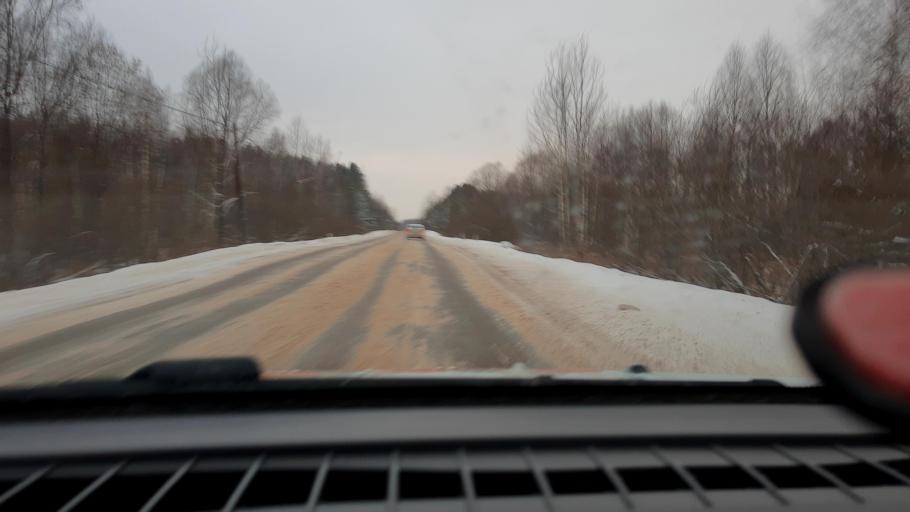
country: RU
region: Nizjnij Novgorod
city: Kstovo
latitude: 56.2779
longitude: 44.3522
